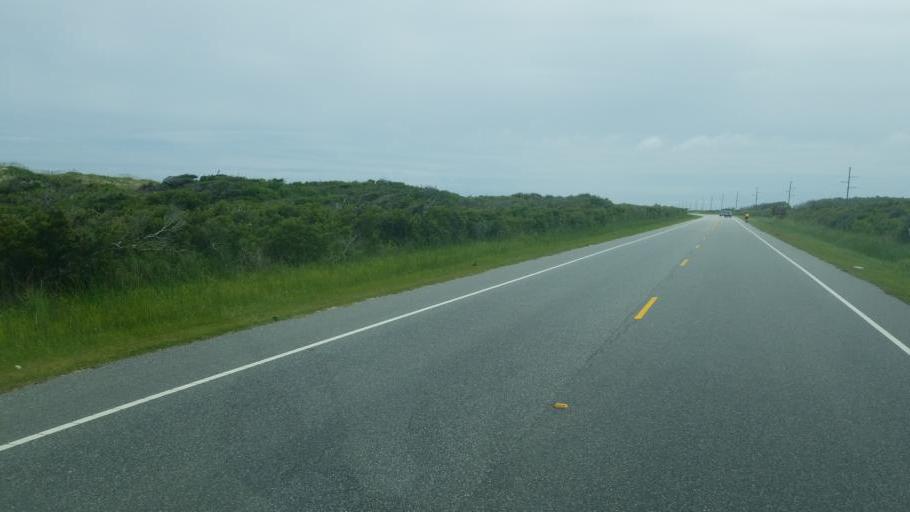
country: US
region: North Carolina
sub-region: Dare County
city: Wanchese
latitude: 35.8352
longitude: -75.5608
